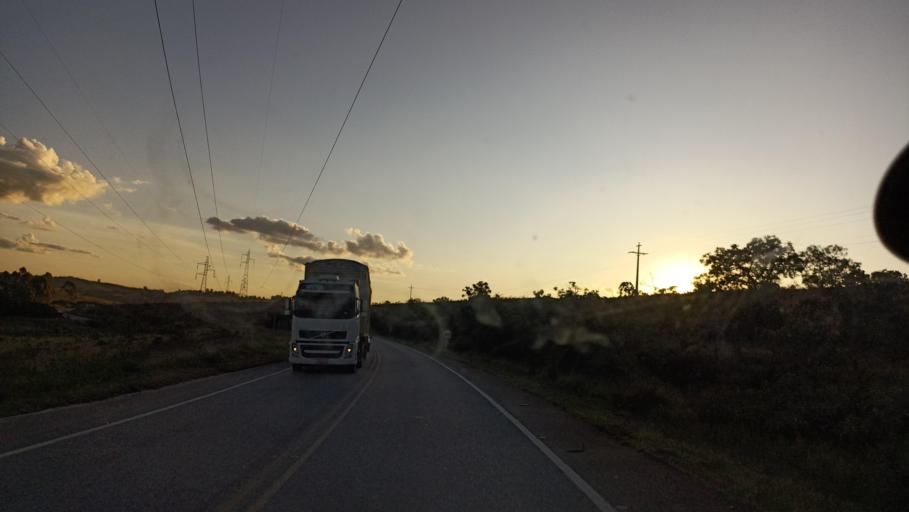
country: BR
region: Minas Gerais
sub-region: Sao Joao Del Rei
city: Sao Joao del Rei
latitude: -21.2259
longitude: -44.3728
